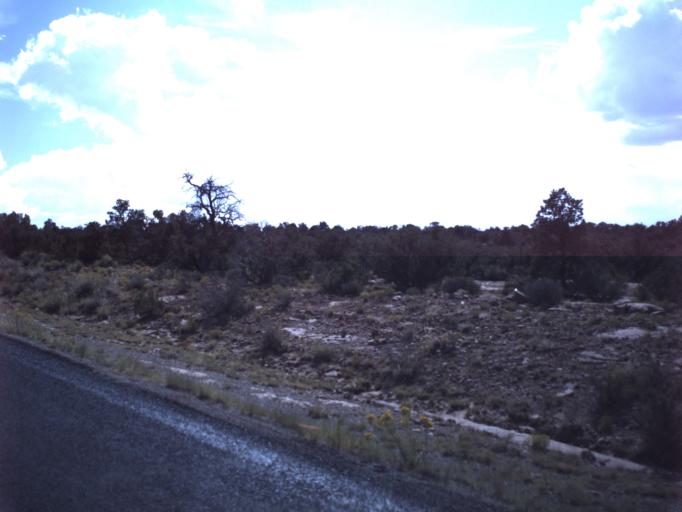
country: US
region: Utah
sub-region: Grand County
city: Moab
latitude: 38.6078
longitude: -109.8172
